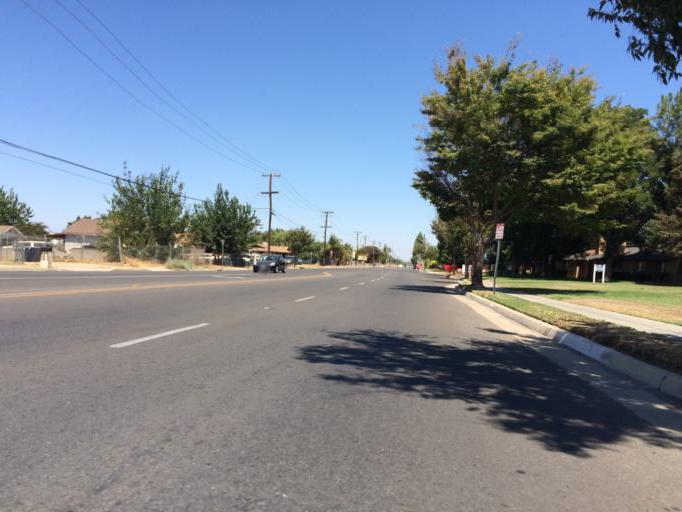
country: US
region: California
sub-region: Fresno County
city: Fresno
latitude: 36.7178
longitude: -119.7456
